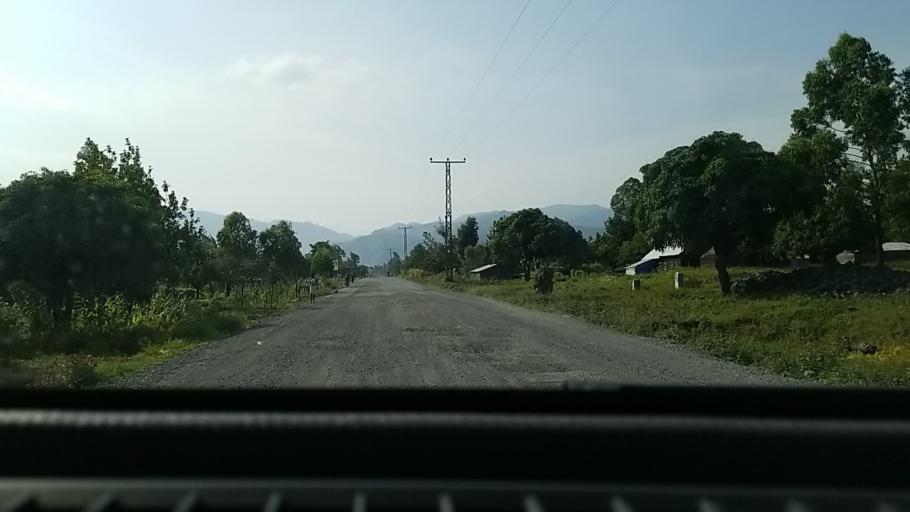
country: CD
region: Nord Kivu
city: Sake
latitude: -1.5775
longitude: 29.0742
